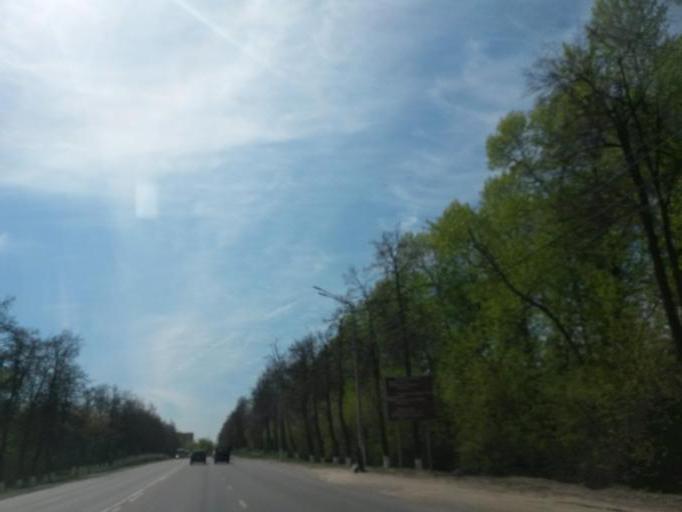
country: RU
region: Moskovskaya
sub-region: Podol'skiy Rayon
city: Podol'sk
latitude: 55.4552
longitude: 37.5552
